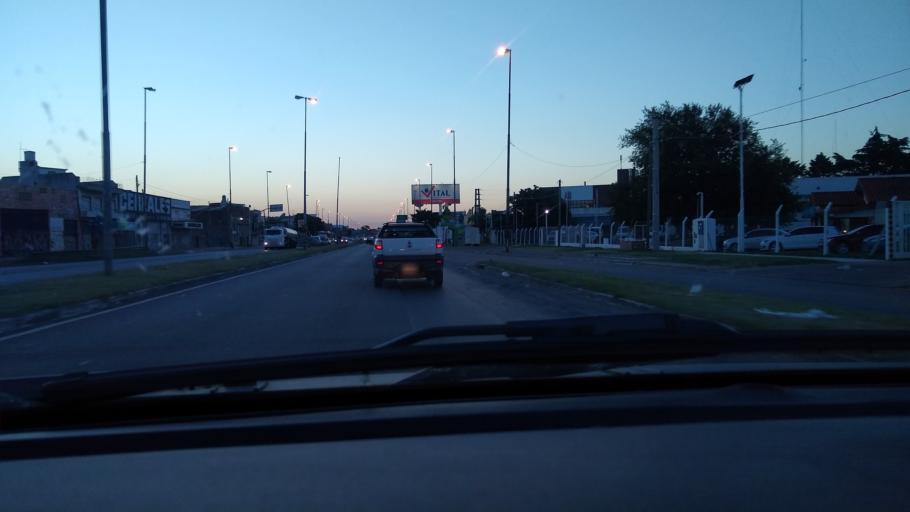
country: AR
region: Buenos Aires
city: San Justo
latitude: -34.6834
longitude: -58.5678
